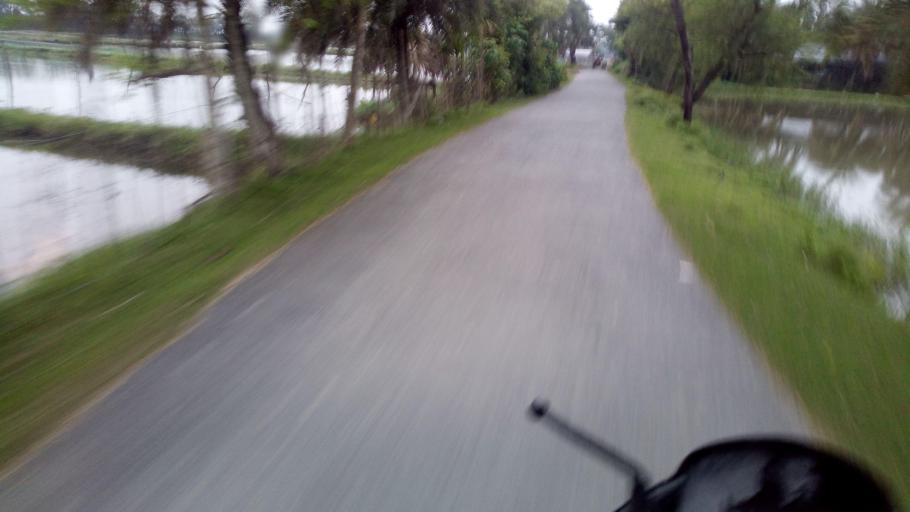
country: BD
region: Khulna
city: Phultala
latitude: 22.7645
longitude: 89.4071
